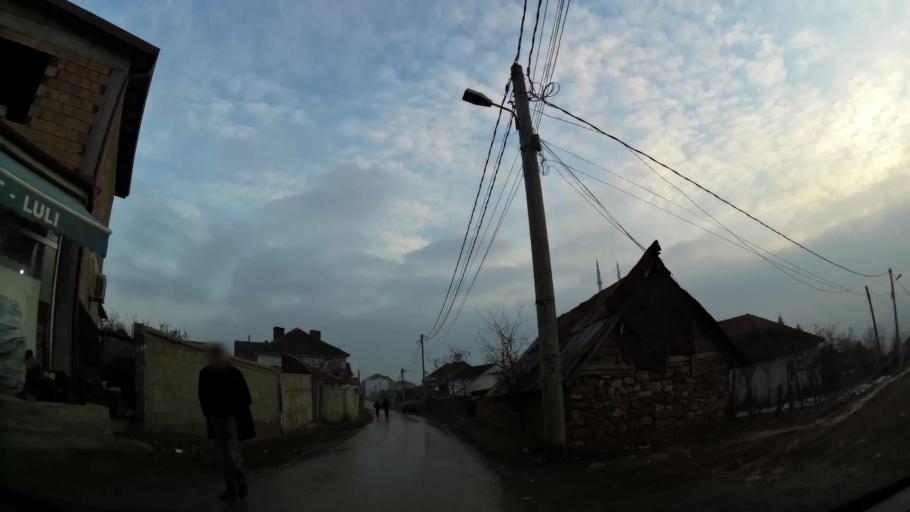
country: MK
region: Aracinovo
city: Arachinovo
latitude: 42.0306
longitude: 21.5584
